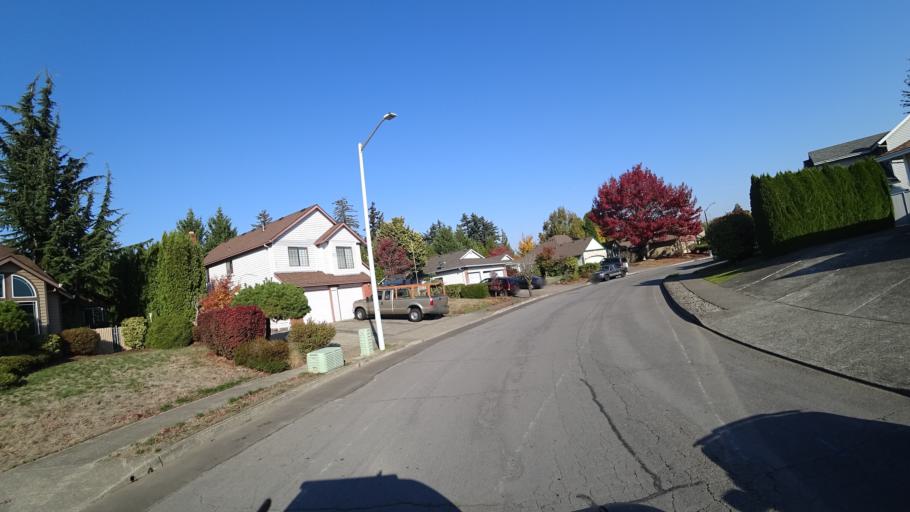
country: US
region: Oregon
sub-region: Multnomah County
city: Wood Village
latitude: 45.5178
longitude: -122.4294
